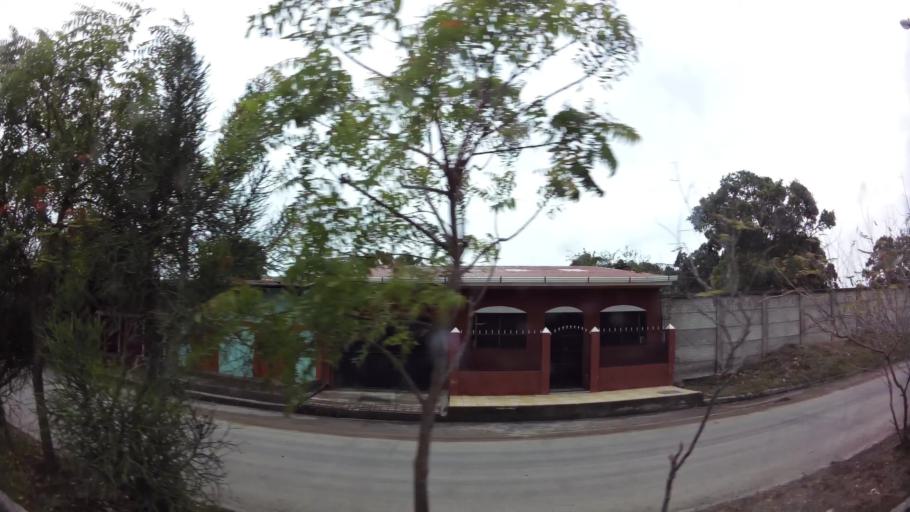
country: NI
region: Granada
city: Granada
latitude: 11.9277
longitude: -85.9427
